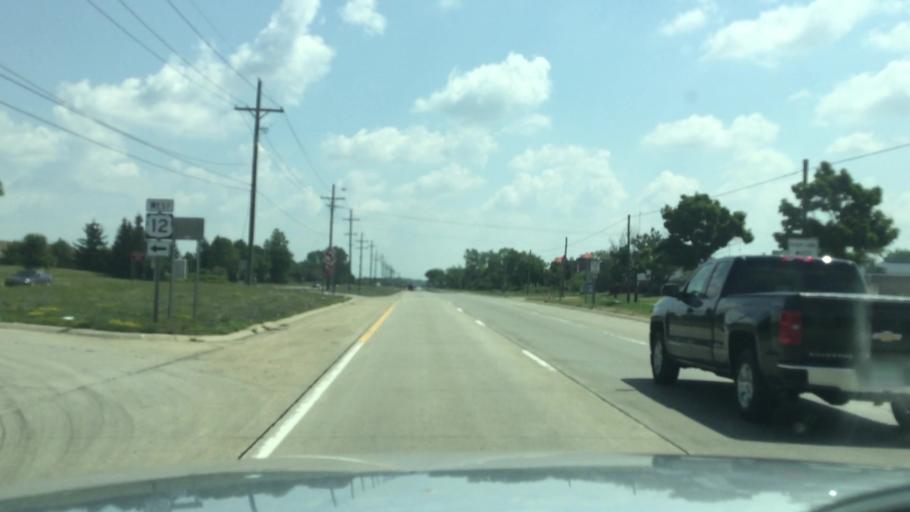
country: US
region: Michigan
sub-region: Wayne County
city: Canton
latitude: 42.2647
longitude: -83.5131
